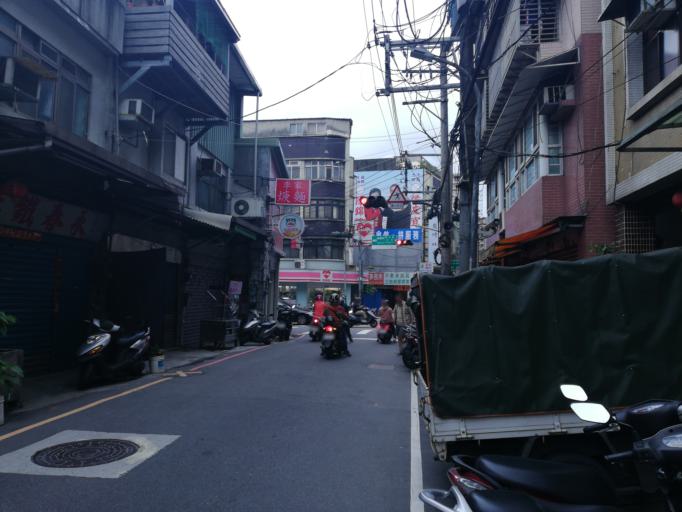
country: TW
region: Taipei
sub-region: Taipei
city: Banqiao
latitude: 24.9978
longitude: 121.5021
